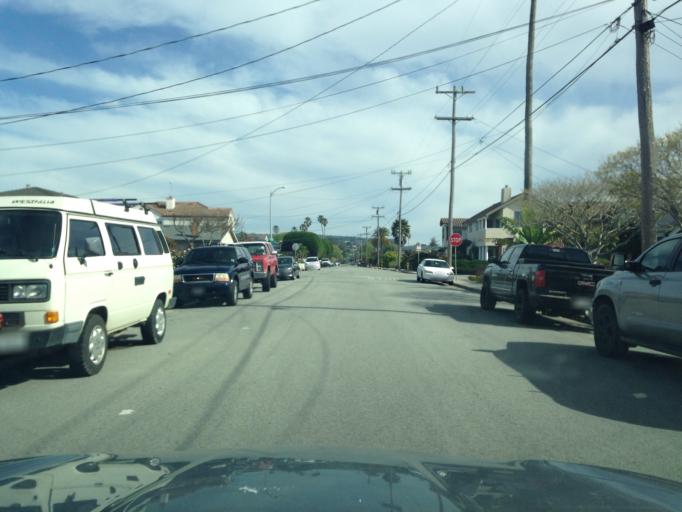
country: US
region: California
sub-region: Santa Cruz County
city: Santa Cruz
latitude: 36.9516
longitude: -122.0456
